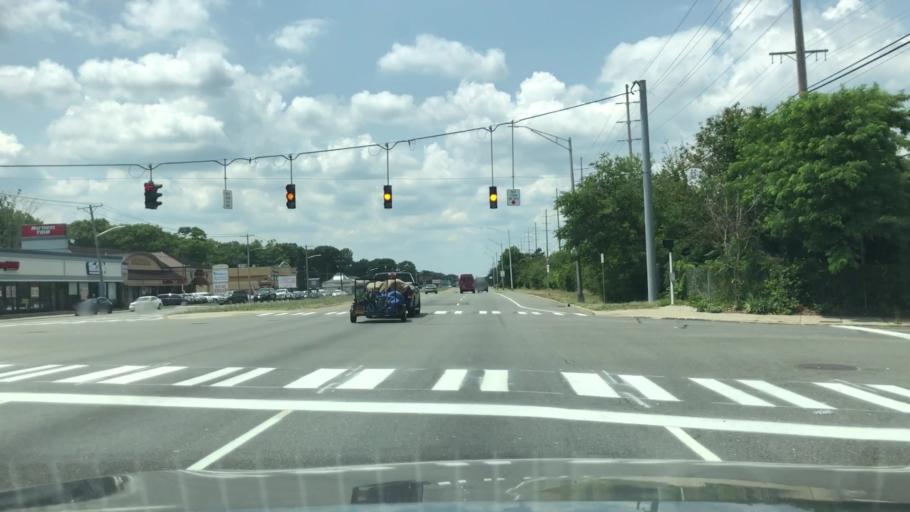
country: US
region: New York
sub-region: Nassau County
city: Massapequa Park
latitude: 40.6781
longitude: -73.4480
